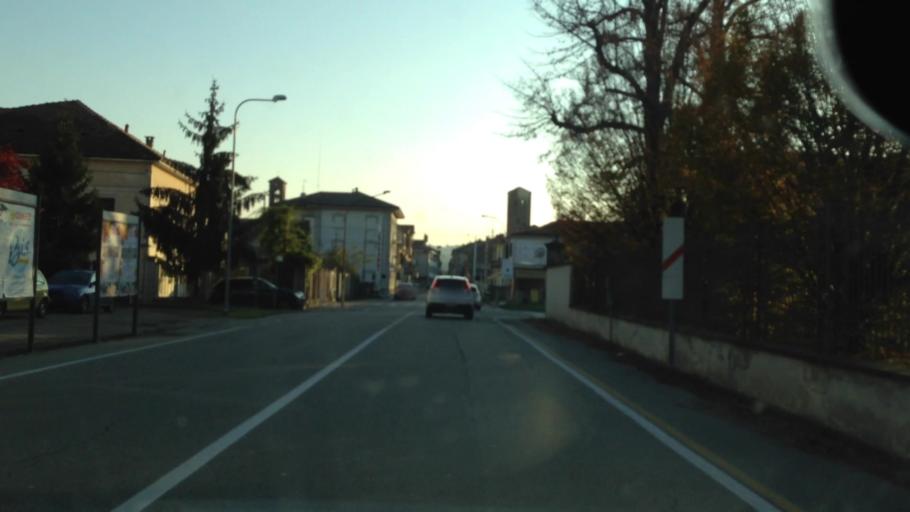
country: IT
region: Piedmont
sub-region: Provincia di Vercelli
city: Crescentino
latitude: 45.1952
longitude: 8.1037
